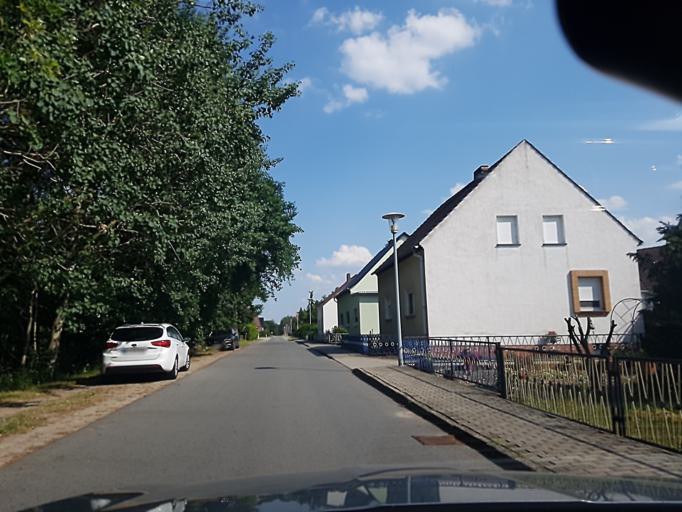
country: DE
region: Brandenburg
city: Ruckersdorf
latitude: 51.5626
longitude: 13.5553
